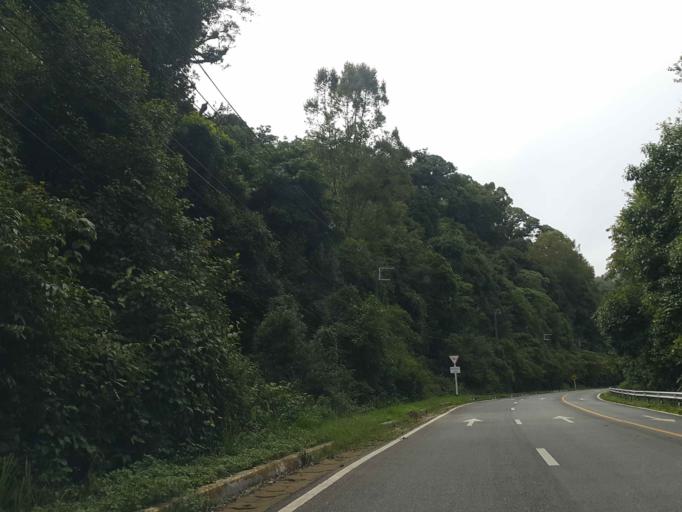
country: TH
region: Chiang Mai
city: Mae Chaem
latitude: 18.5604
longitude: 98.4833
